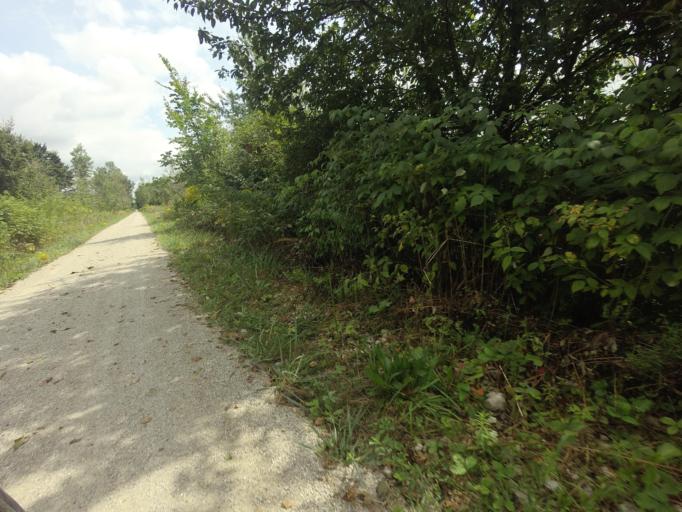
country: CA
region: Ontario
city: North Perth
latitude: 43.5662
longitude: -80.9527
